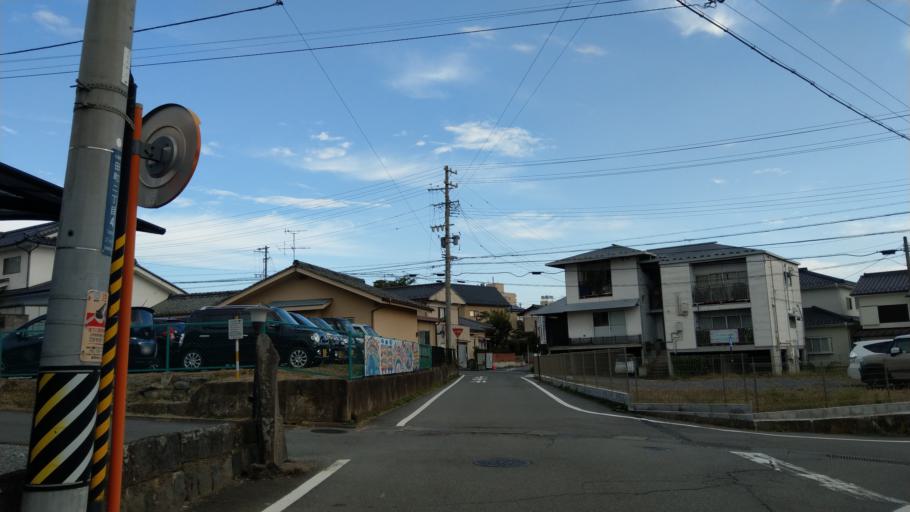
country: JP
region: Nagano
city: Komoro
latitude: 36.3317
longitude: 138.4230
